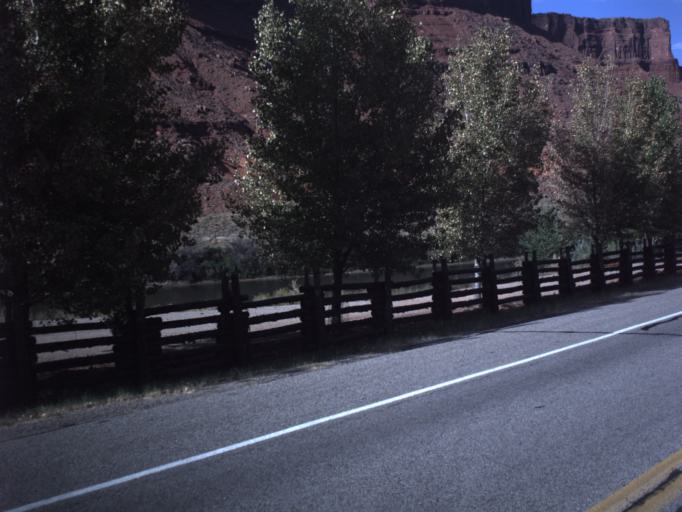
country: US
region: Utah
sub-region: Grand County
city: Moab
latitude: 38.6792
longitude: -109.4449
